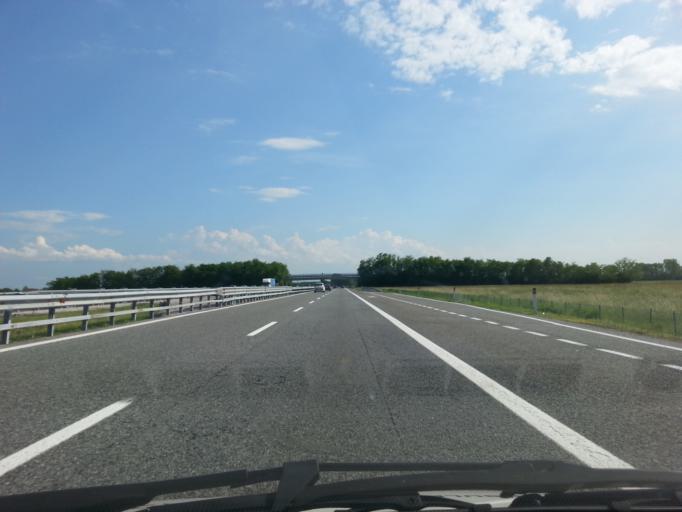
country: IT
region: Piedmont
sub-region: Provincia di Cuneo
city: Caramagna Piemonte
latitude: 44.7606
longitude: 7.7506
